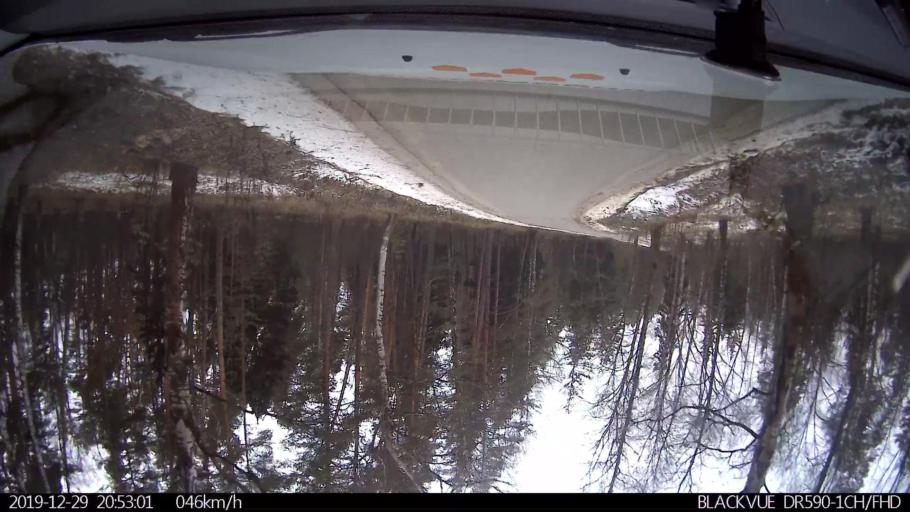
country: RU
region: Nizjnij Novgorod
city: Afonino
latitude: 56.1736
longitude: 43.9889
